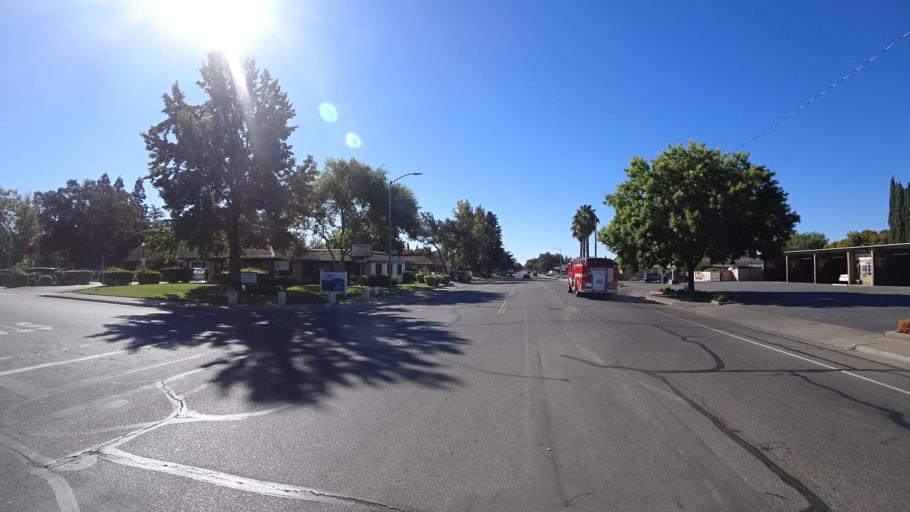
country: US
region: California
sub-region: Sacramento County
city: Elk Grove
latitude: 38.4058
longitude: -121.3715
